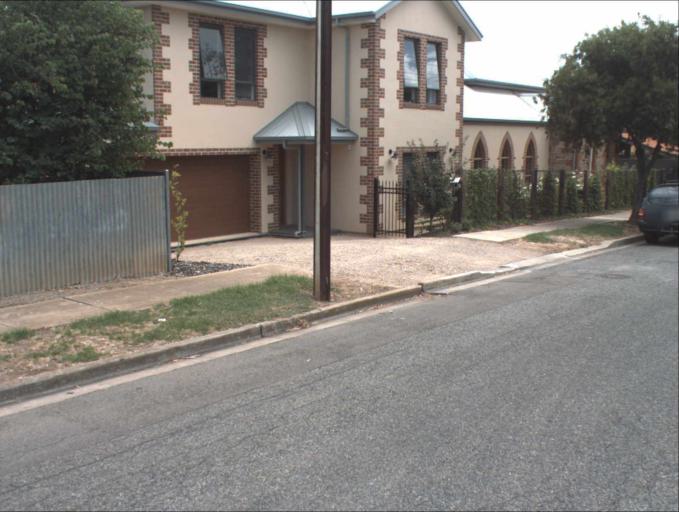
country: AU
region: South Australia
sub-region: Salisbury
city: Ingle Farm
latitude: -34.8483
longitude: 138.6234
